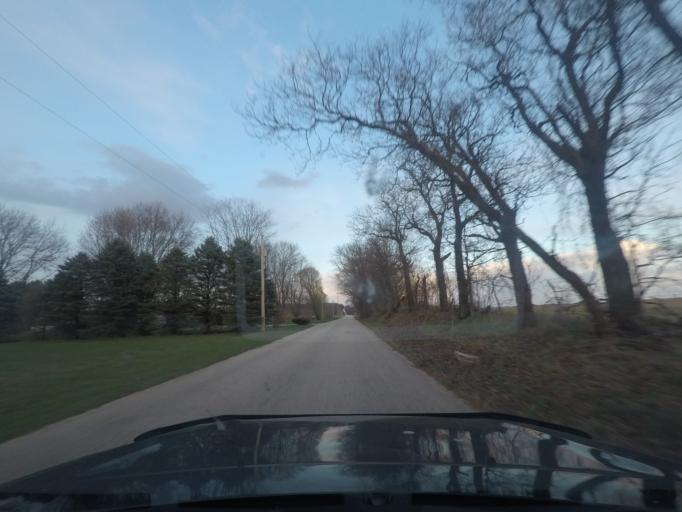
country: US
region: Indiana
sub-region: LaPorte County
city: Kingsford Heights
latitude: 41.4620
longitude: -86.7214
